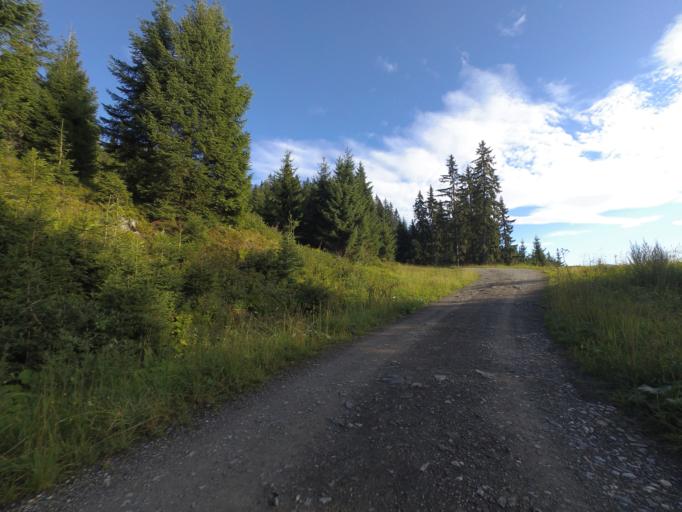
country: AT
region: Salzburg
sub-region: Politischer Bezirk Sankt Johann im Pongau
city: Goldegg
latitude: 47.3511
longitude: 13.1040
